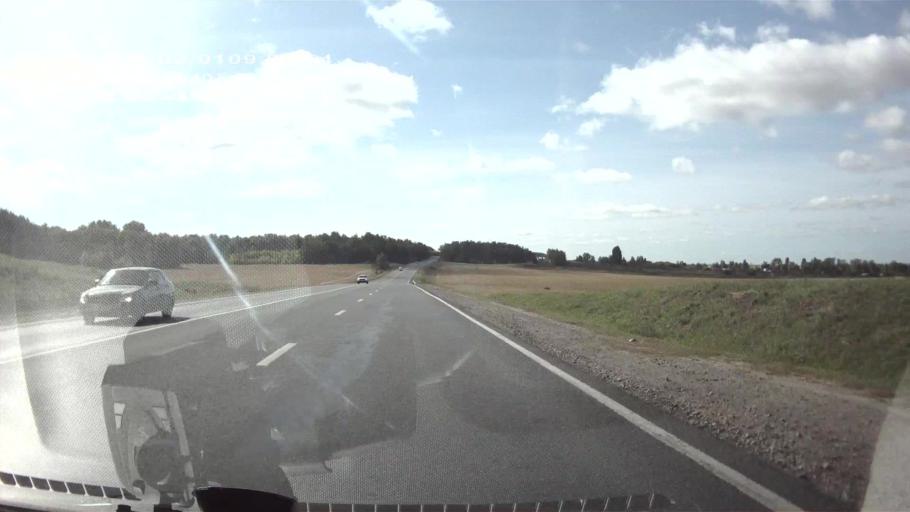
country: RU
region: Ulyanovsk
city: Krasnyy Gulyay
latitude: 54.0857
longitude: 48.2311
